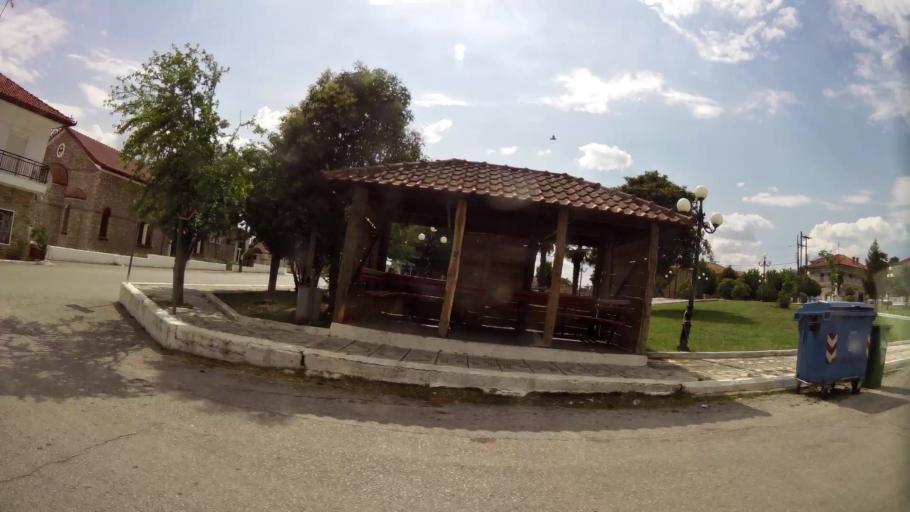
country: GR
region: Central Macedonia
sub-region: Nomos Pierias
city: Makrygialos
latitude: 40.4155
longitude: 22.6036
